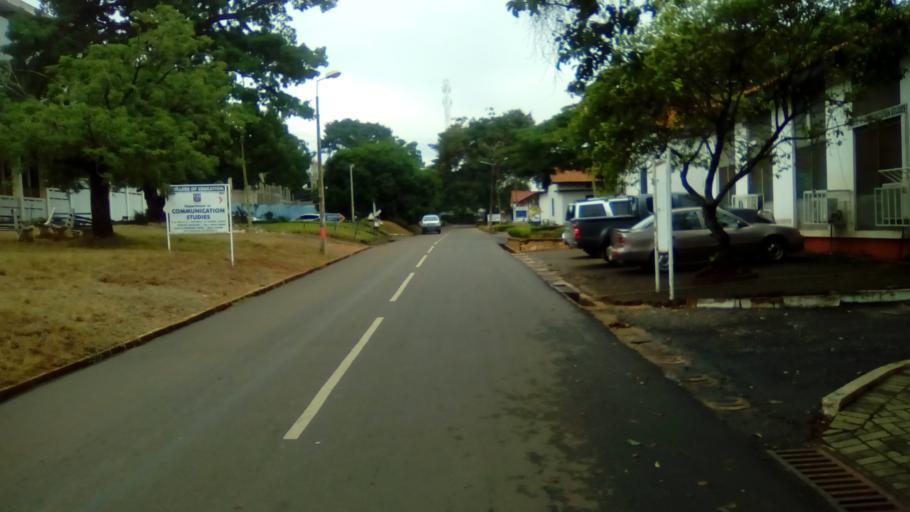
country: GH
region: Greater Accra
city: Medina Estates
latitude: 5.6515
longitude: -0.1814
